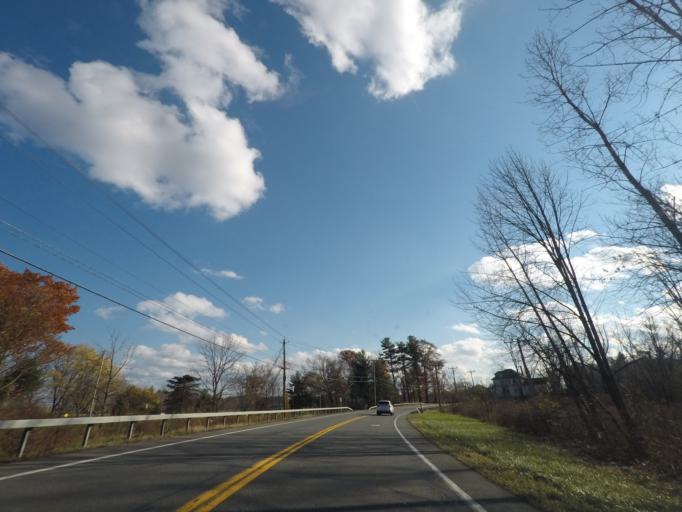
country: US
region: New York
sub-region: Schenectady County
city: Niskayuna
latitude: 42.8160
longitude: -73.8663
